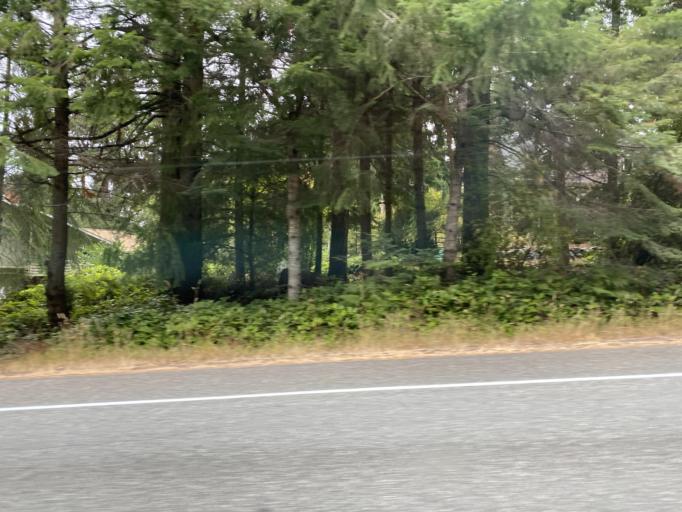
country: US
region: Washington
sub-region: Island County
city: Coupeville
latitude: 48.2198
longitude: -122.6427
